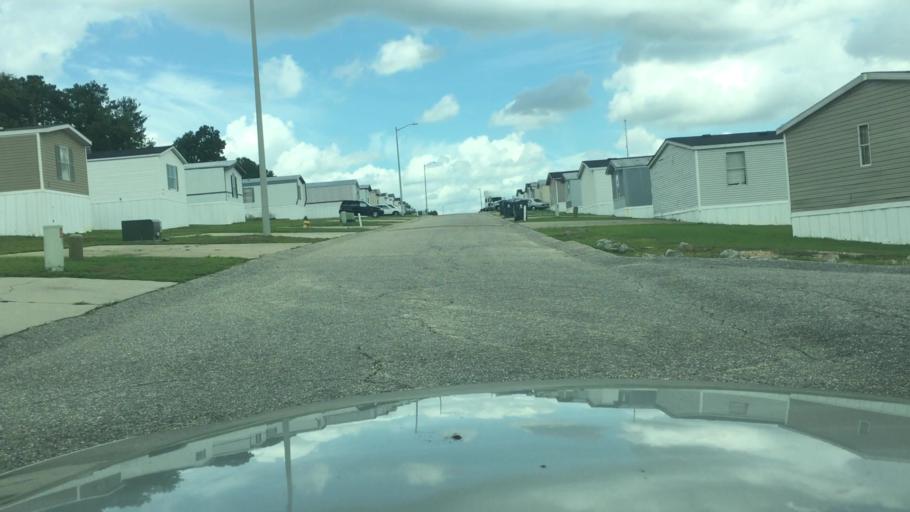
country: US
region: North Carolina
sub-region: Cumberland County
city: Hope Mills
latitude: 35.0371
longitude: -78.9780
